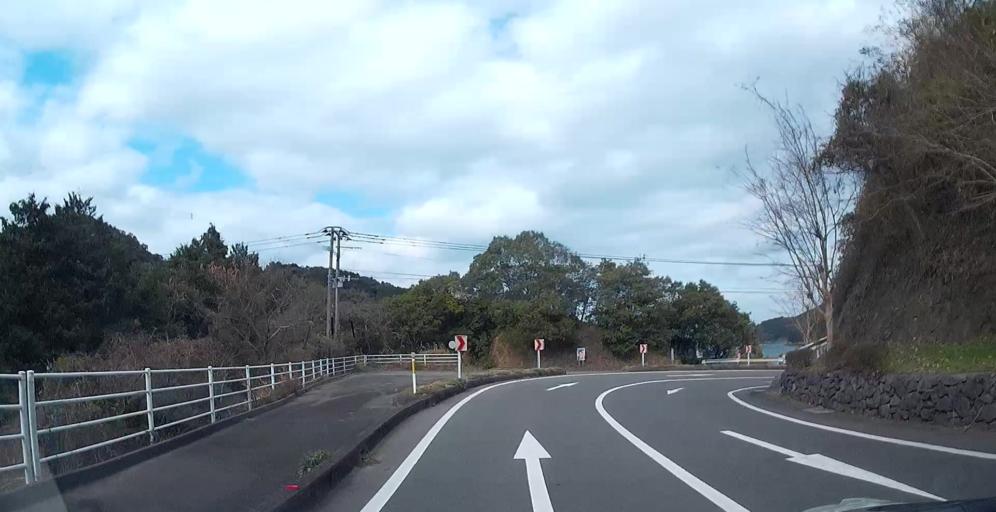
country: JP
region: Kumamoto
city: Minamata
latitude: 32.3267
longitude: 130.4765
